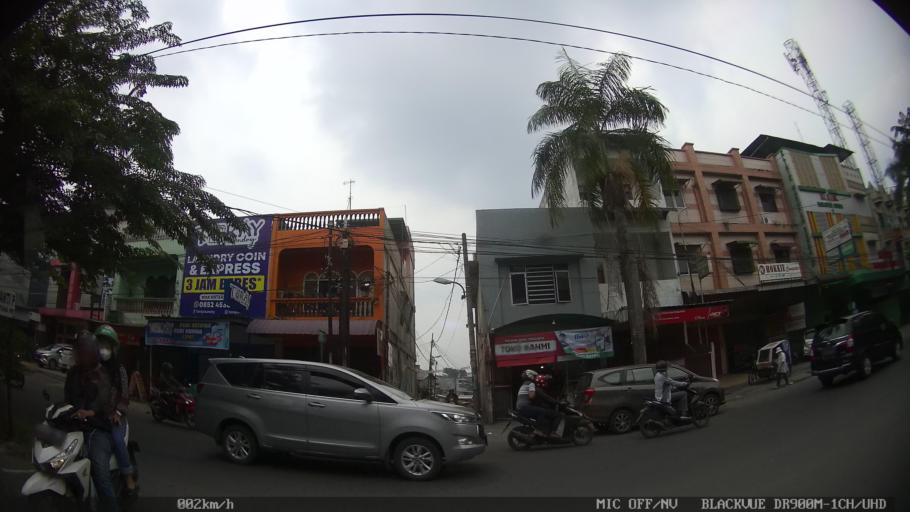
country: ID
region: North Sumatra
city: Medan
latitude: 3.5613
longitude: 98.6895
